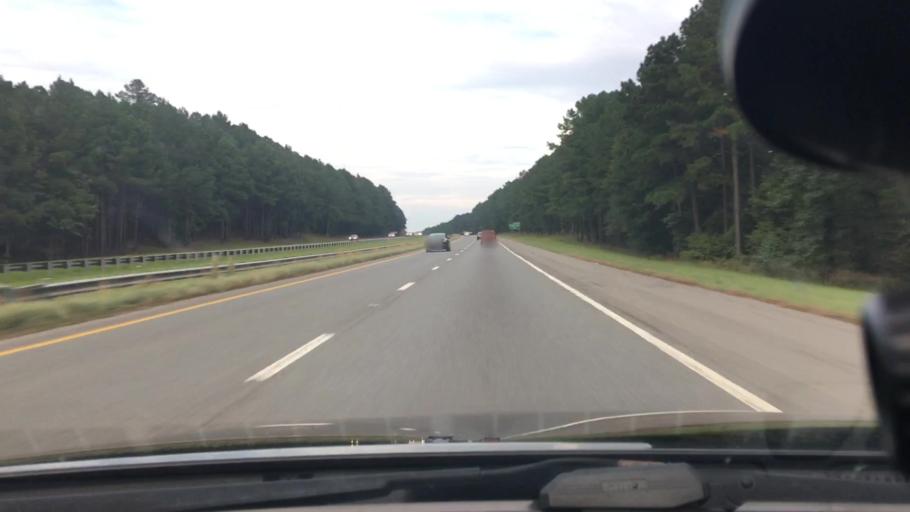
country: US
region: North Carolina
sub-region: Chatham County
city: Farmville
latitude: 35.5443
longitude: -79.1678
